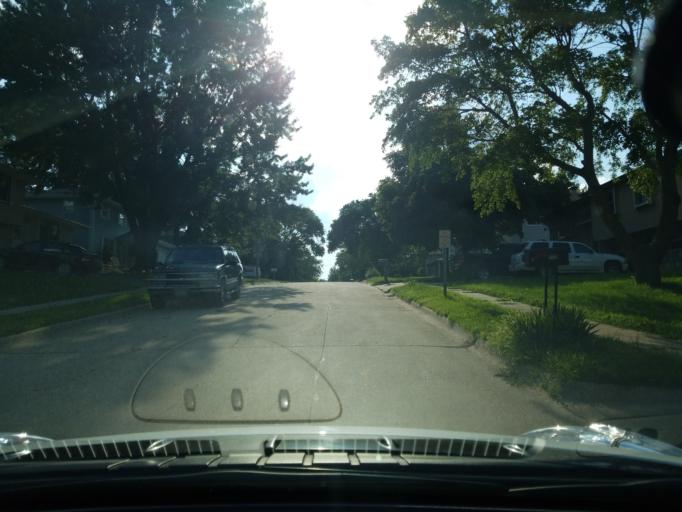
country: US
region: Nebraska
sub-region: Sarpy County
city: Offutt Air Force Base
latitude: 41.1332
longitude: -95.9602
